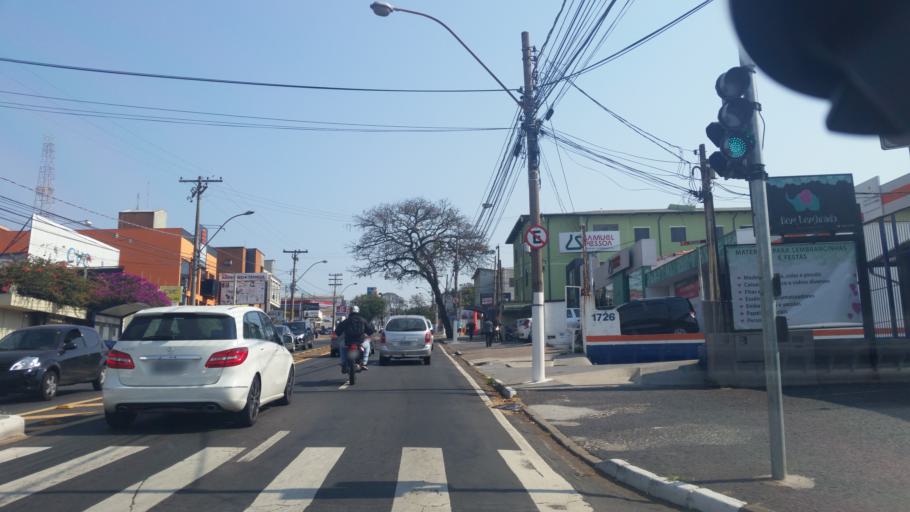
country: BR
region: Sao Paulo
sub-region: Campinas
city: Campinas
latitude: -22.8945
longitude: -47.0744
